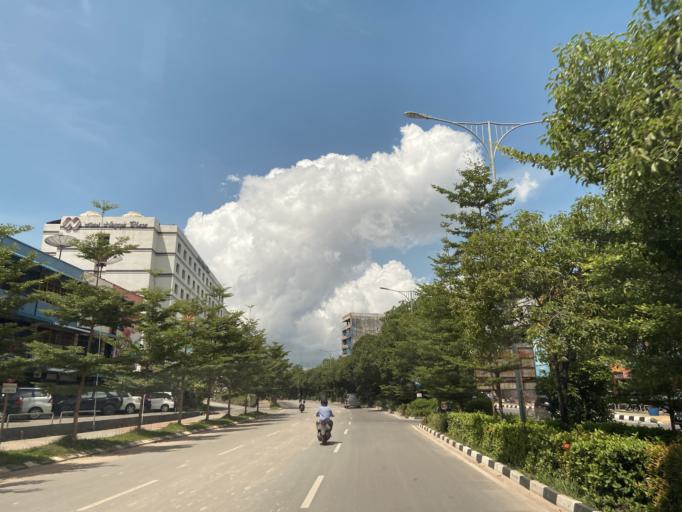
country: SG
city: Singapore
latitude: 1.1468
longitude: 104.0103
